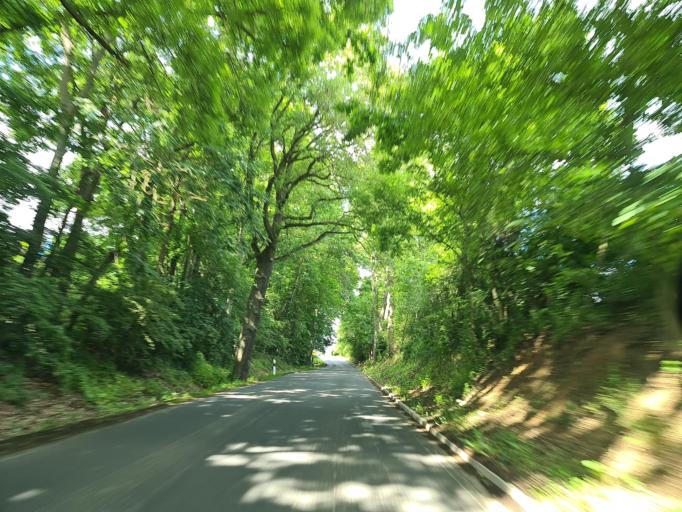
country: DE
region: Saxony
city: Syrau
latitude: 50.5134
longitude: 12.0921
